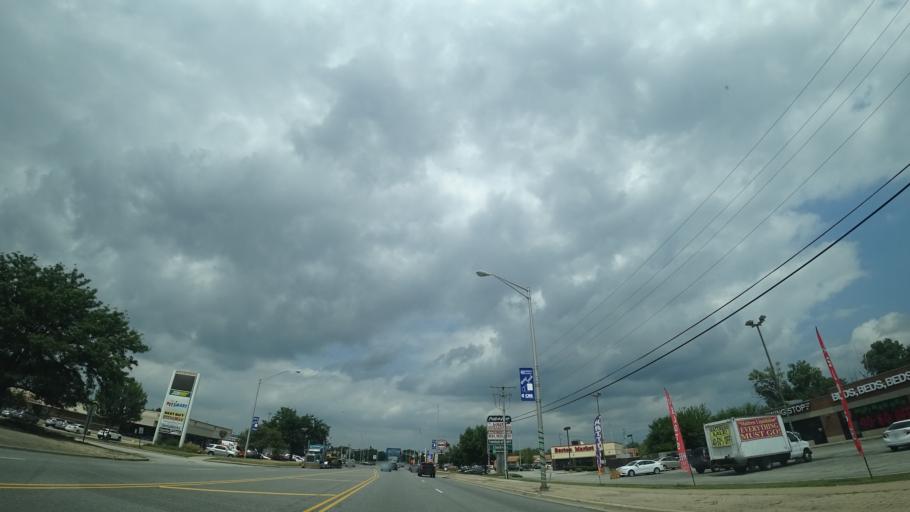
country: US
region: Illinois
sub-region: Cook County
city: Crestwood
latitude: 41.6517
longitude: -87.7382
